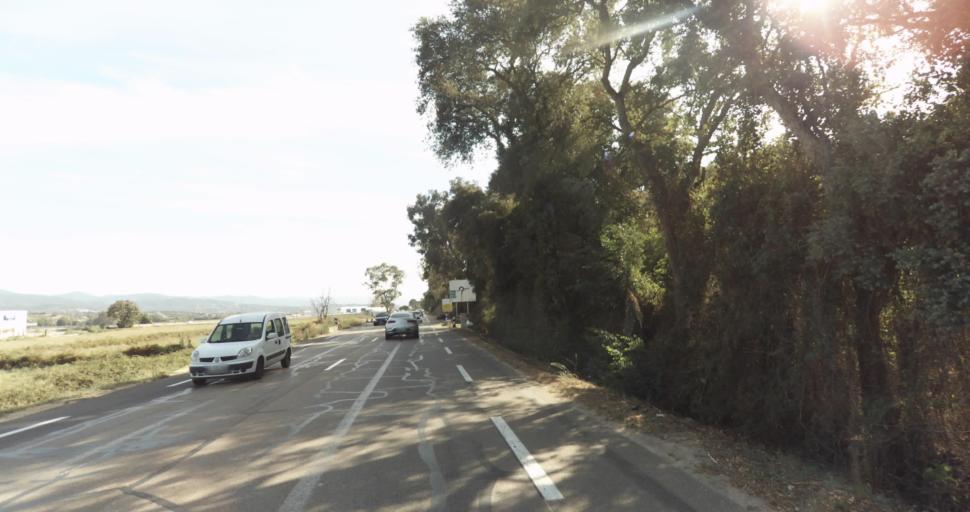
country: FR
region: Corsica
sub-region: Departement de la Corse-du-Sud
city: Afa
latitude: 41.9354
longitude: 8.8030
